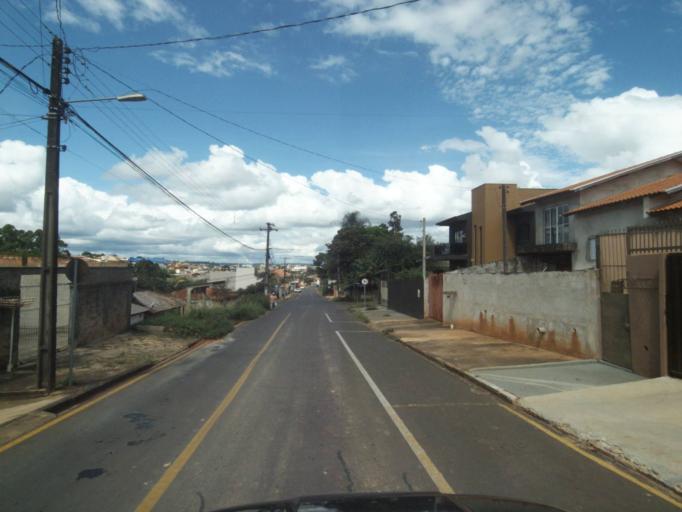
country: BR
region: Parana
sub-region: Telemaco Borba
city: Telemaco Borba
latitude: -24.3210
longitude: -50.6314
